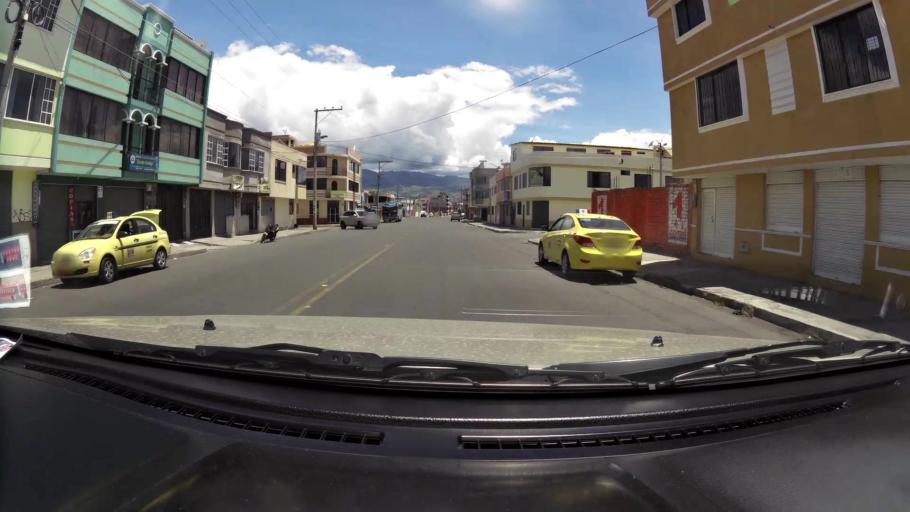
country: EC
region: Chimborazo
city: Riobamba
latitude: -1.6855
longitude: -78.6385
